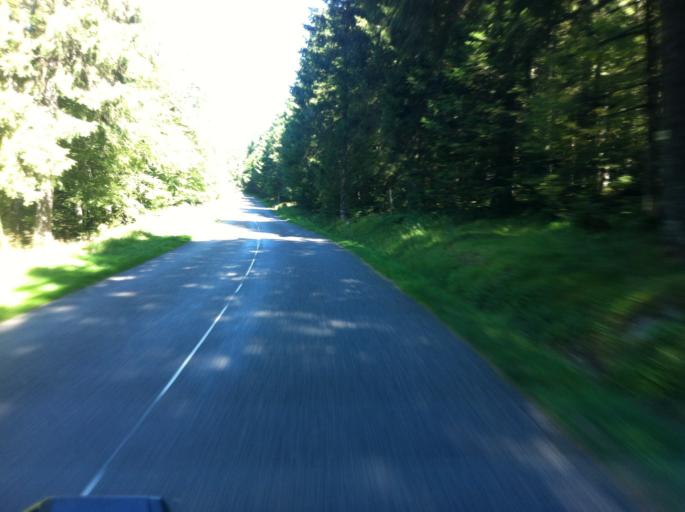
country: FR
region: Alsace
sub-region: Departement du Haut-Rhin
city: Soultzeren
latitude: 48.1251
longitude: 7.0731
